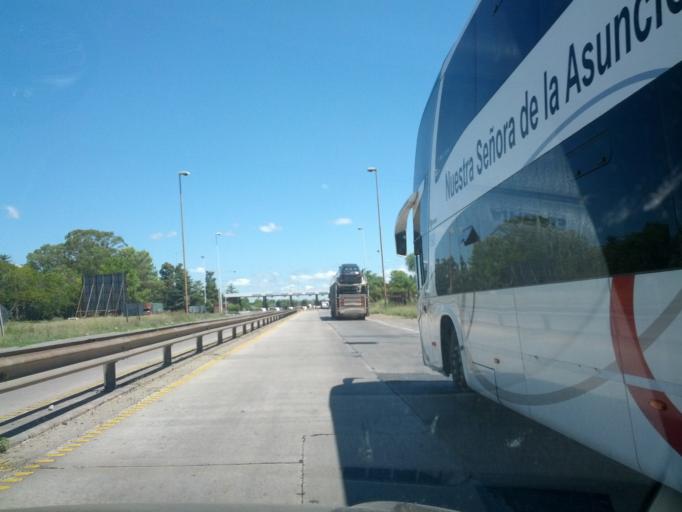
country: AR
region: Buenos Aires
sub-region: Partido de Zarate
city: Zarate
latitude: -34.1164
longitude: -59.0095
